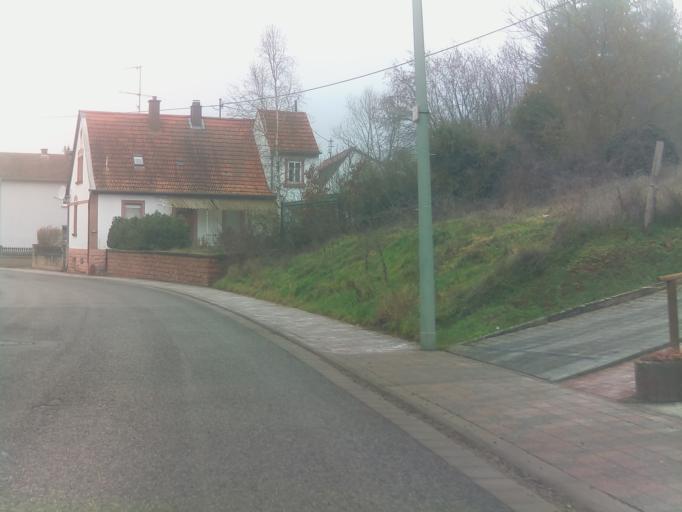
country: DE
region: Rheinland-Pfalz
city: Neuhemsbach
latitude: 49.5244
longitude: 7.9091
